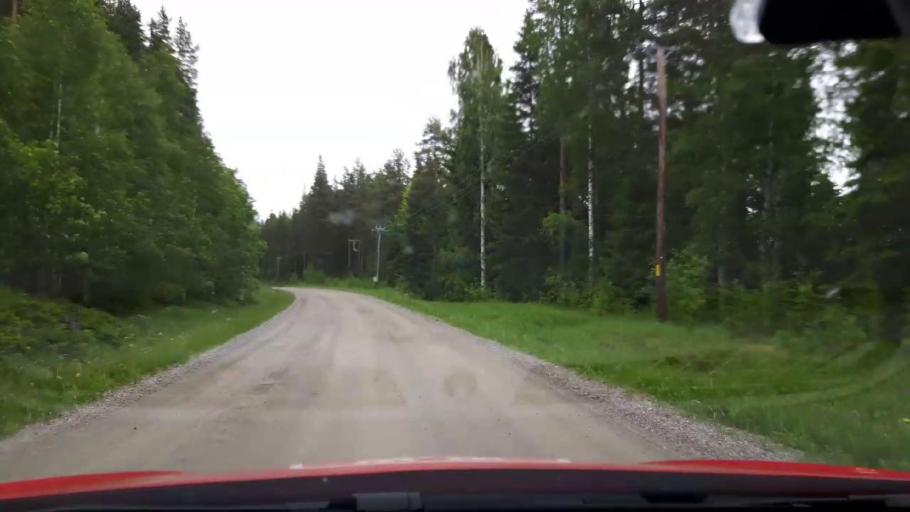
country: SE
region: Jaemtland
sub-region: Ragunda Kommun
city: Hammarstrand
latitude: 63.1805
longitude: 16.1612
